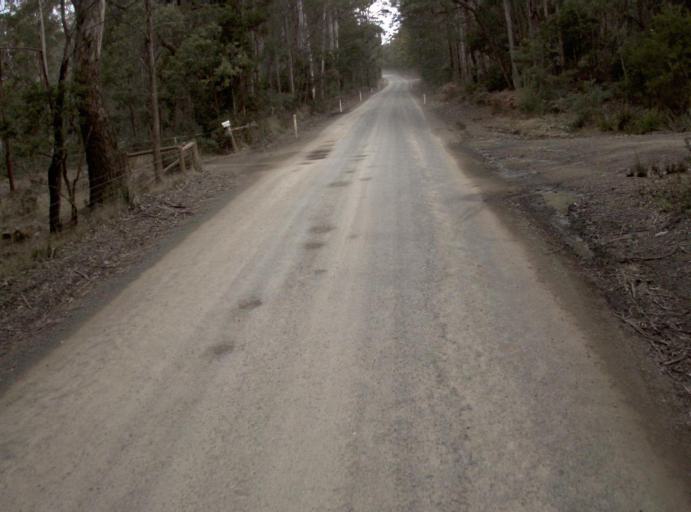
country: AU
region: Tasmania
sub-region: Launceston
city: Newstead
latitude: -41.3612
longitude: 147.2287
